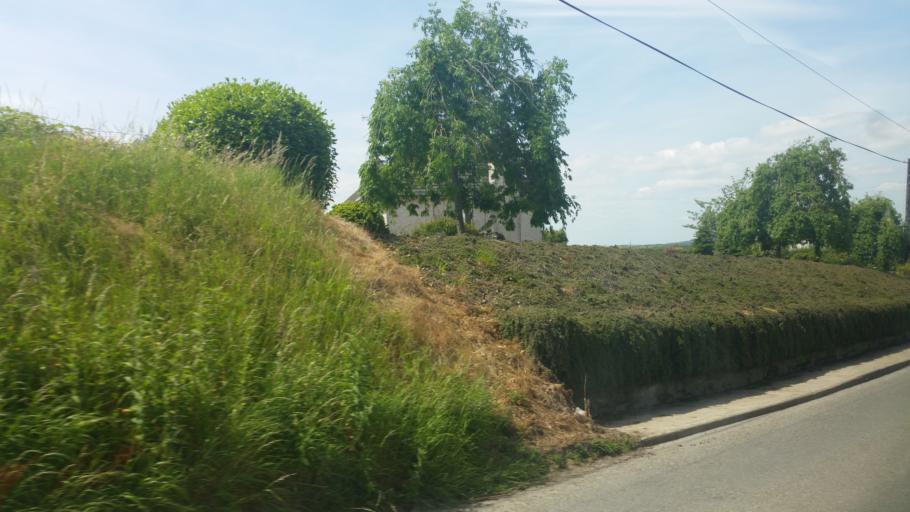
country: IE
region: Leinster
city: Lusk
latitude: 53.5319
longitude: -6.1750
